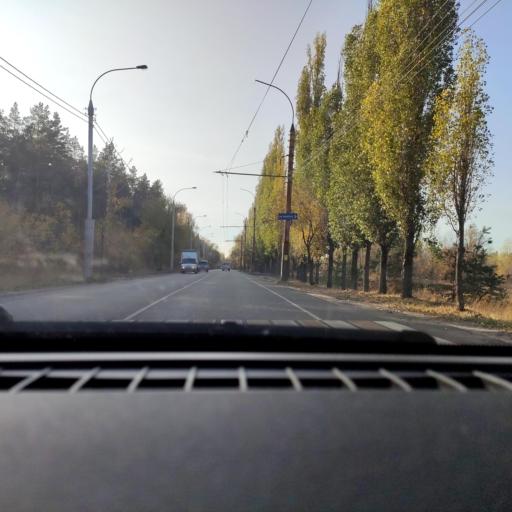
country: RU
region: Voronezj
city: Somovo
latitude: 51.7096
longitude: 39.2921
